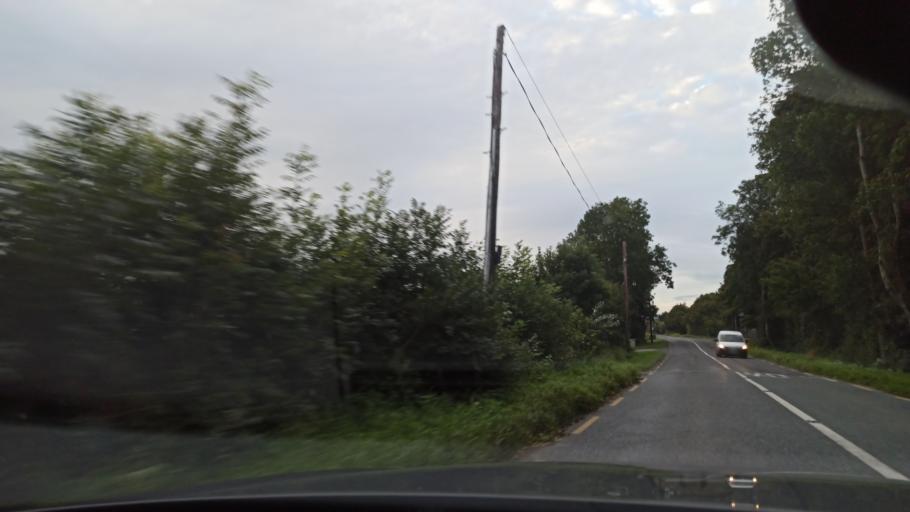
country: IE
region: Munster
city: Cashel
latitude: 52.4901
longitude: -7.8592
